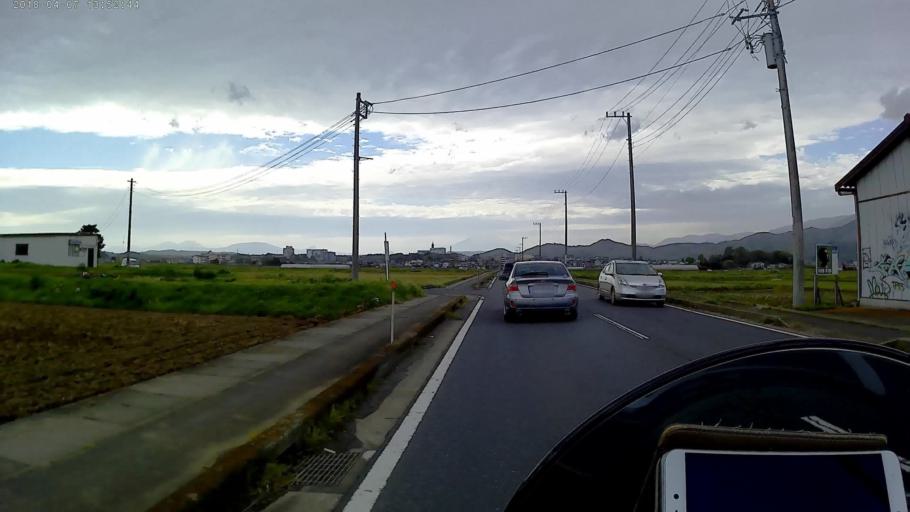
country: JP
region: Kanagawa
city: Isehara
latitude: 35.3672
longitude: 139.2959
